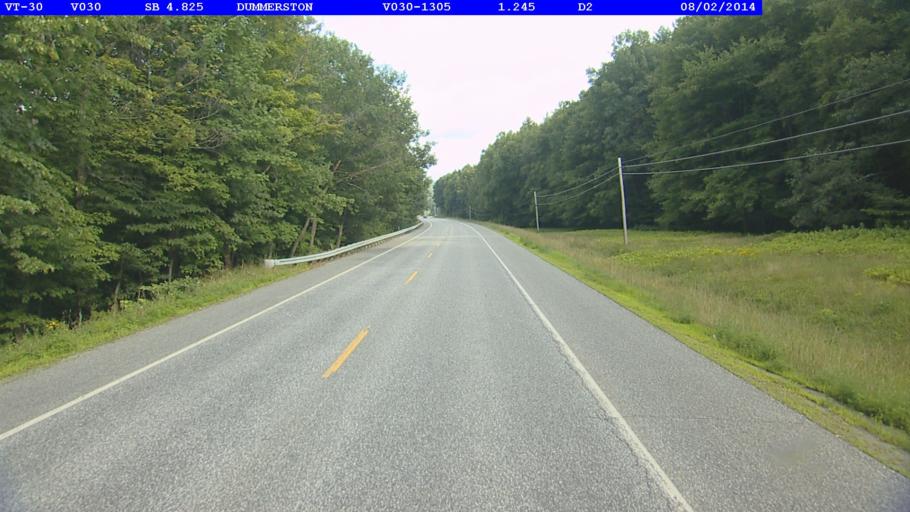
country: US
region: Vermont
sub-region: Windham County
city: West Brattleboro
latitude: 42.9124
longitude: -72.6095
